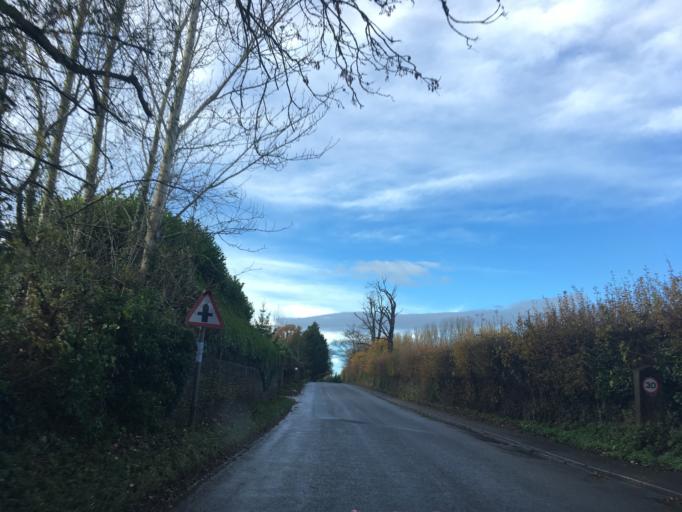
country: GB
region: England
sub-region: South Gloucestershire
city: Winterbourne
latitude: 51.5147
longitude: -2.4695
